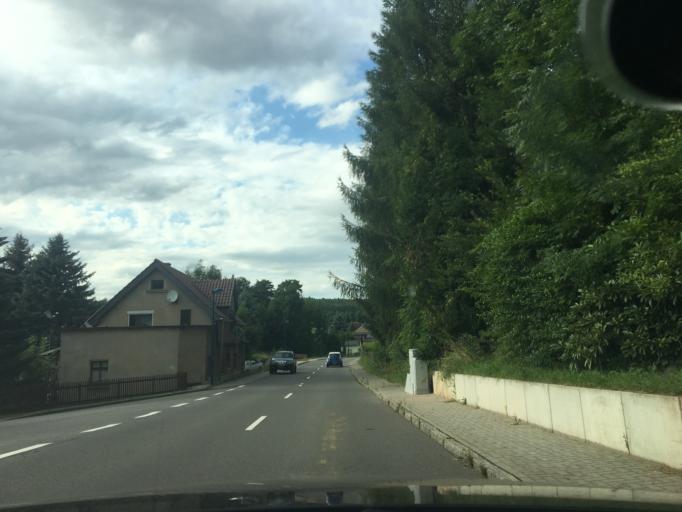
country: DE
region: Saxony
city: Oelsnitz
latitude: 50.7142
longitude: 12.6821
